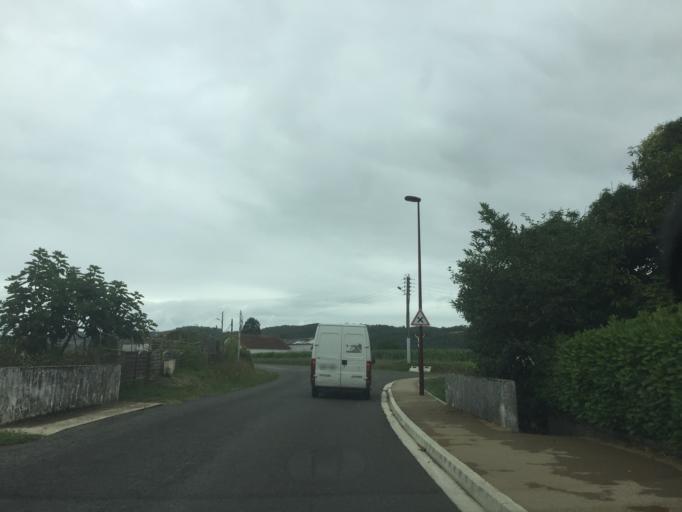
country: FR
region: Midi-Pyrenees
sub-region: Departement des Hautes-Pyrenees
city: Rabastens-de-Bigorre
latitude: 43.3357
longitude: 0.2277
